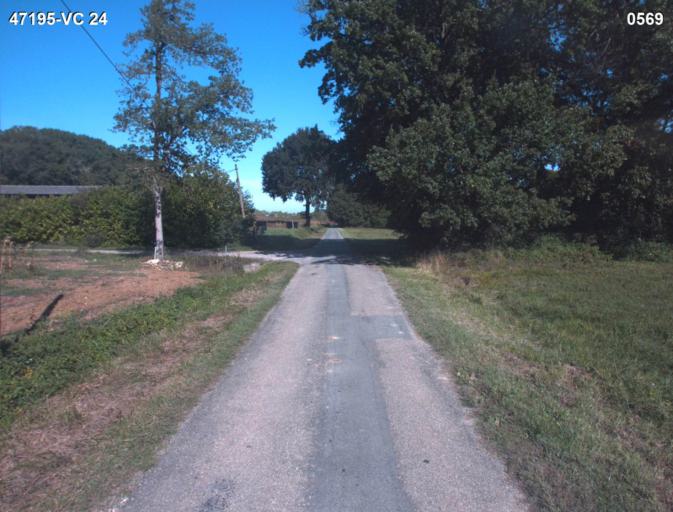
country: FR
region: Aquitaine
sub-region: Departement du Lot-et-Garonne
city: Nerac
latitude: 44.1665
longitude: 0.3630
